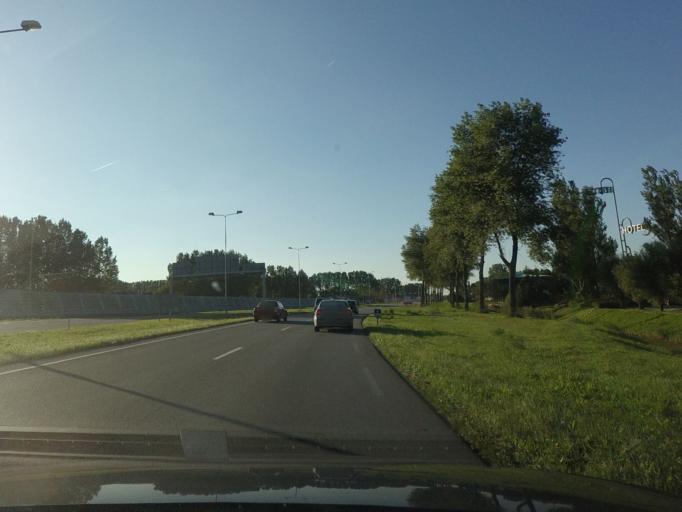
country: NL
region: North Holland
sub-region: Gemeente Haarlemmermeer
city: Hoofddorp
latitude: 52.3161
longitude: 4.6742
